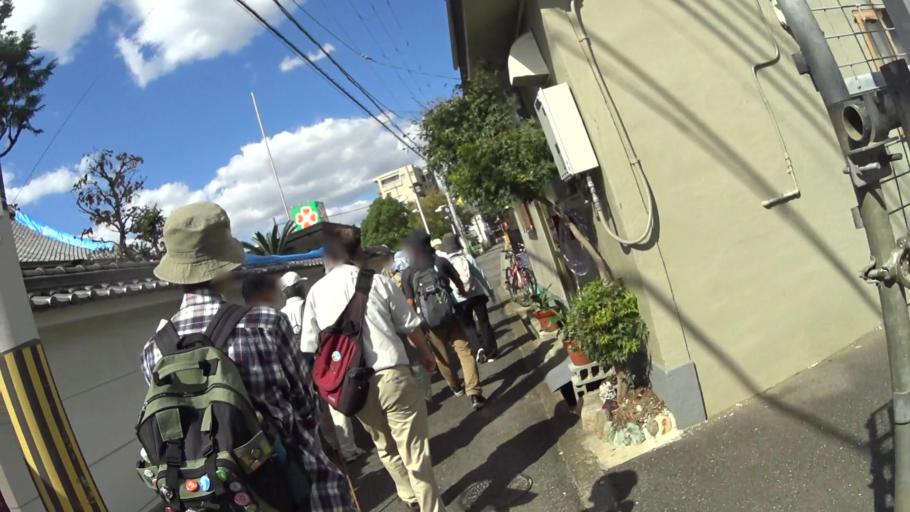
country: JP
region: Osaka
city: Yao
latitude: 34.6495
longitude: 135.5552
